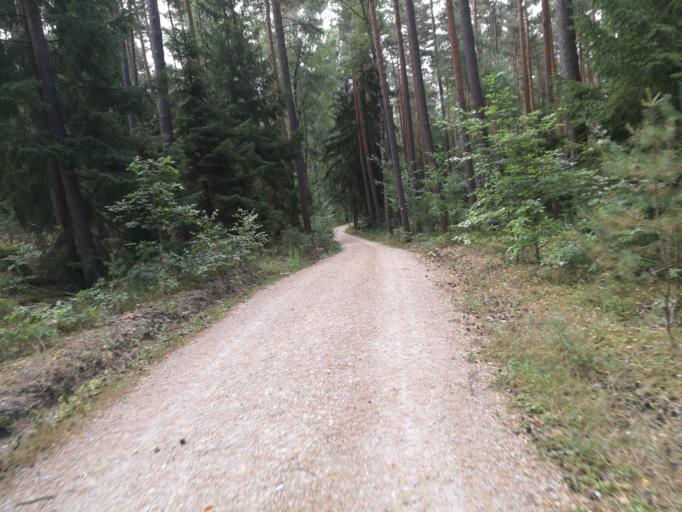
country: DE
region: Bavaria
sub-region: Regierungsbezirk Mittelfranken
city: Seukendorf
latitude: 49.4702
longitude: 10.9206
